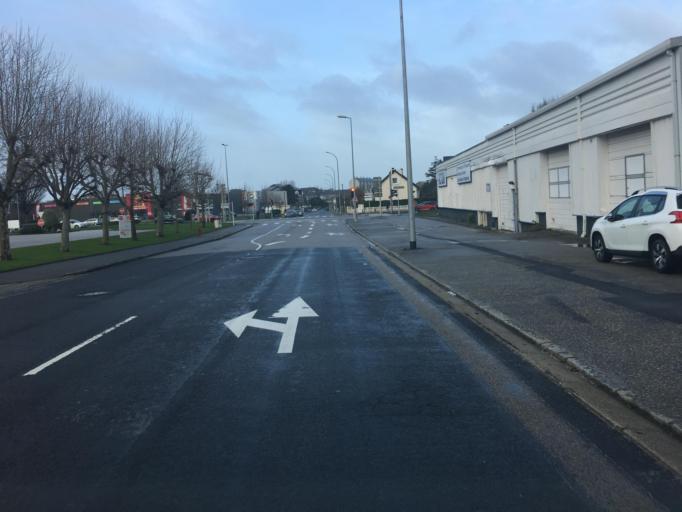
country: FR
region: Lower Normandy
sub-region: Departement de la Manche
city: Cherbourg-Octeville
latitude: 49.6338
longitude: -1.6016
